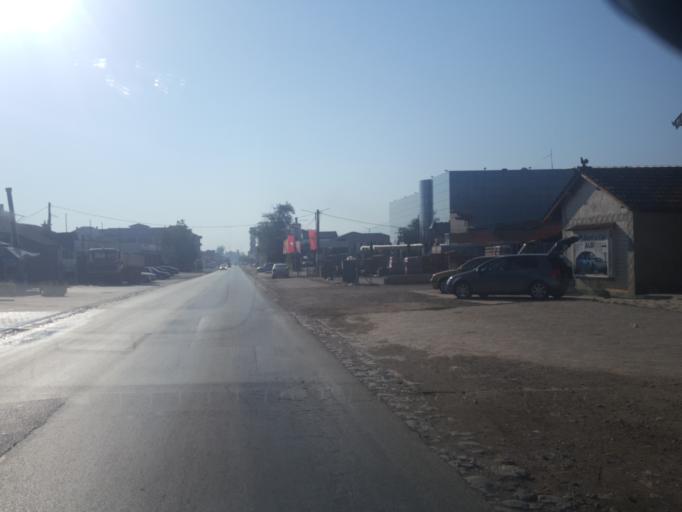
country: XK
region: Gjakova
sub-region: Komuna e Gjakoves
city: Gjakove
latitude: 42.4060
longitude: 20.4090
